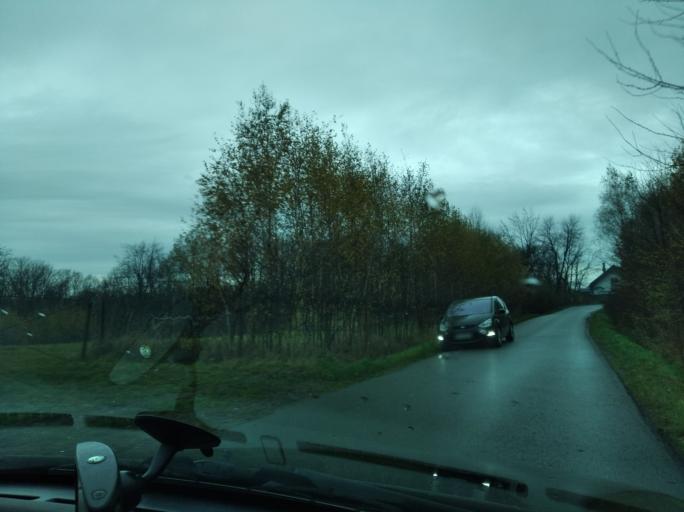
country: PL
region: Subcarpathian Voivodeship
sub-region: Powiat rzeszowski
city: Tyczyn
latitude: 49.9442
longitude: 22.0372
